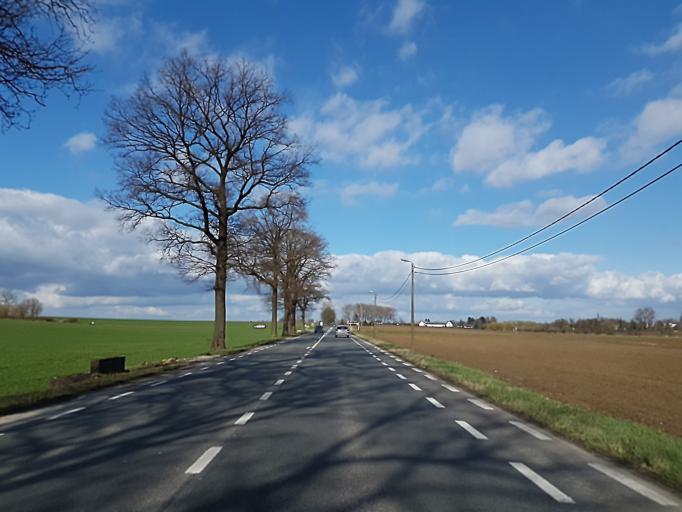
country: BE
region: Wallonia
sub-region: Province du Brabant Wallon
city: Perwez
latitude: 50.6540
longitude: 4.8025
